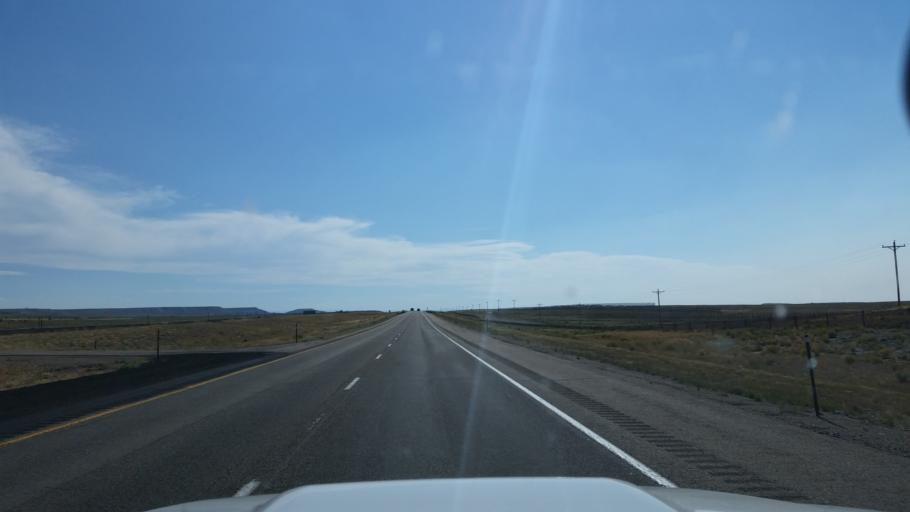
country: US
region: Wyoming
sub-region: Uinta County
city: Lyman
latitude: 41.4638
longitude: -110.0509
